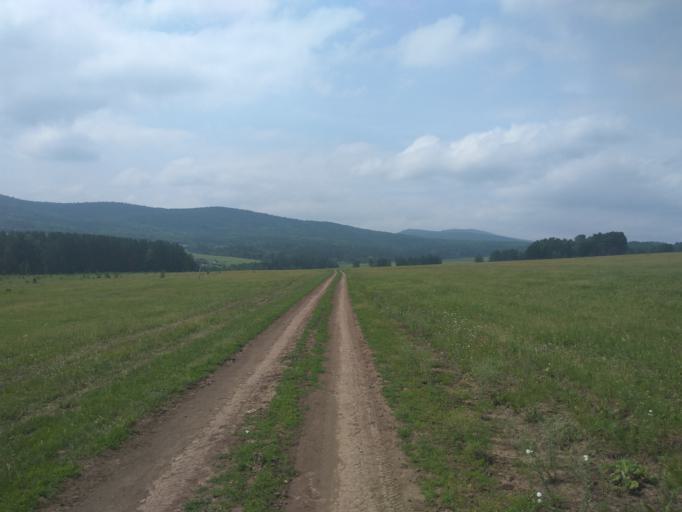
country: RU
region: Krasnoyarskiy
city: Zykovo
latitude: 55.8465
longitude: 93.2090
